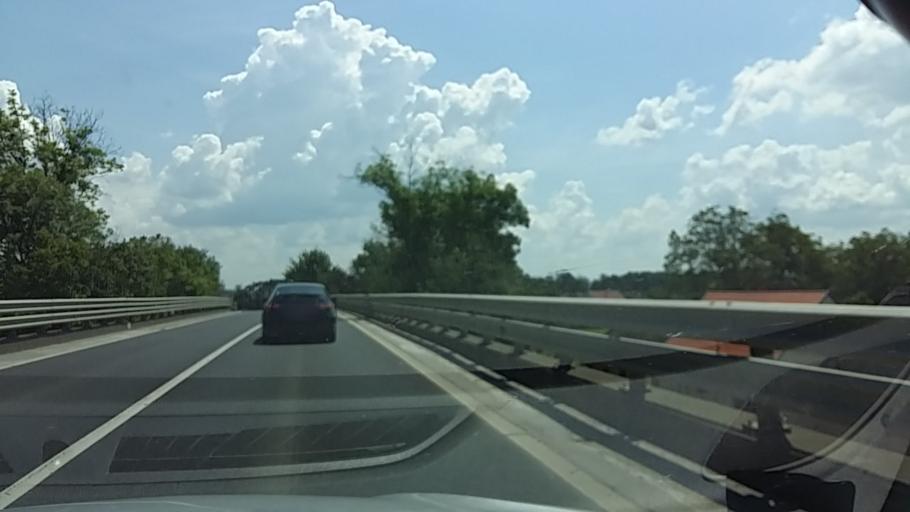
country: AT
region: Burgenland
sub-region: Politischer Bezirk Gussing
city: Heiligenbrunn
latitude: 46.9671
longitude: 16.4282
